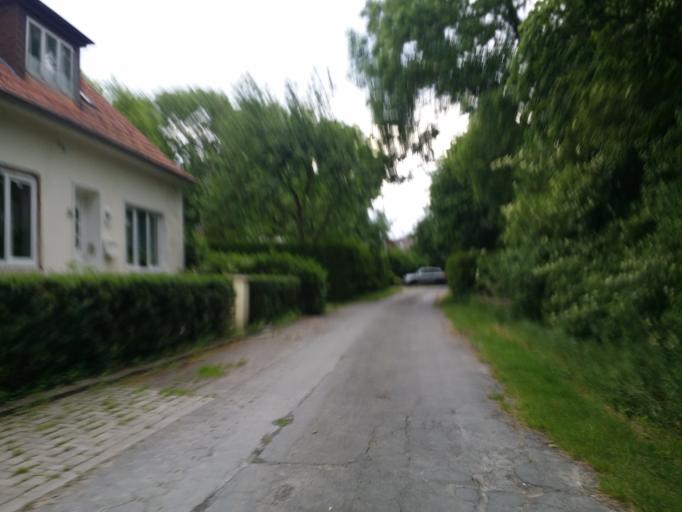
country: DE
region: Lower Saxony
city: Werdum
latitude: 53.6509
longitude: 7.7799
